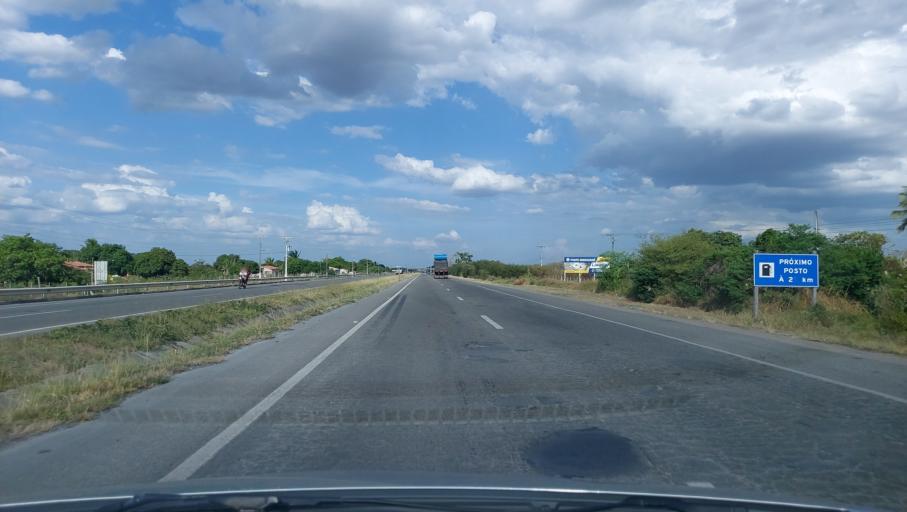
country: BR
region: Bahia
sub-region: Castro Alves
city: Castro Alves
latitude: -12.5497
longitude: -39.4510
